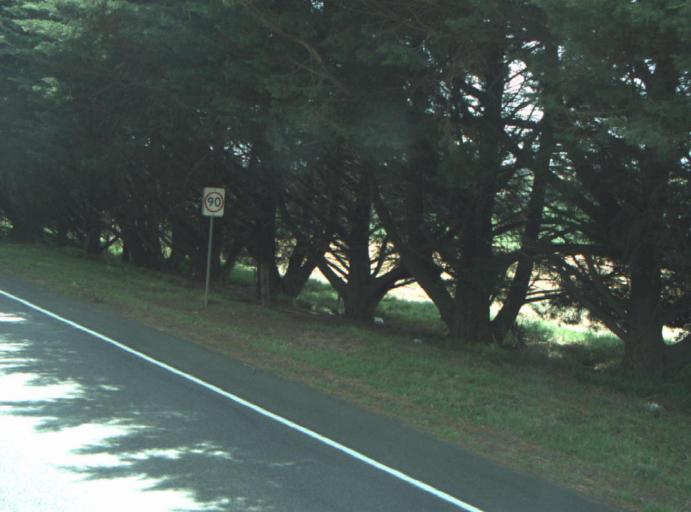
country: AU
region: Victoria
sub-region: Greater Geelong
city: Clifton Springs
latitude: -38.1516
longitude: 144.5919
